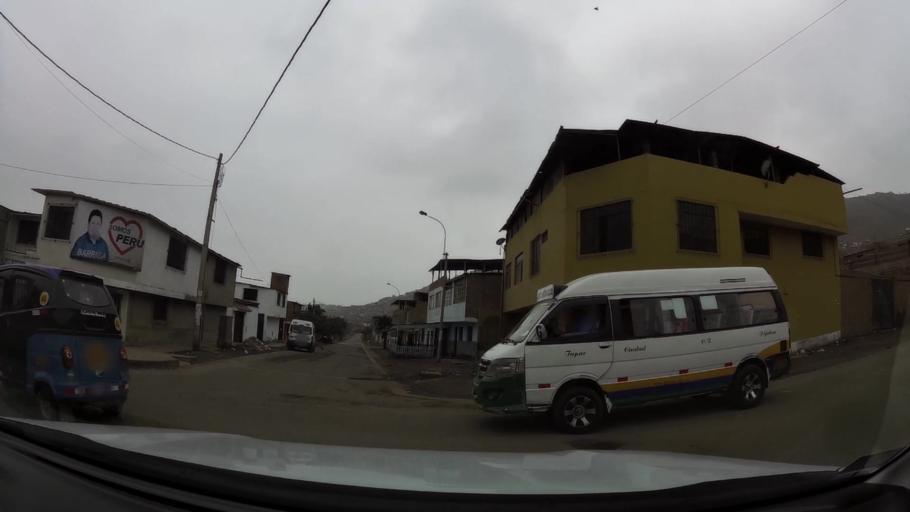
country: PE
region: Lima
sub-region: Lima
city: Surco
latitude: -12.2088
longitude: -76.9118
